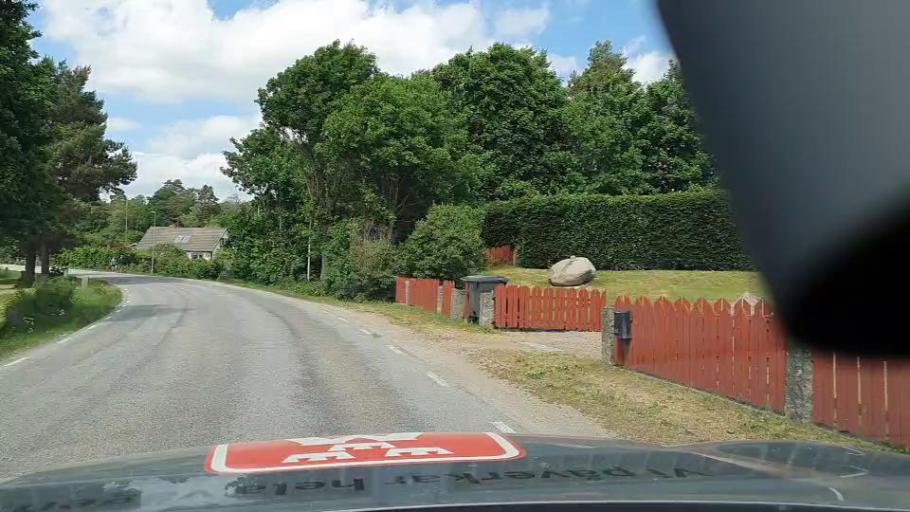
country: SE
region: Blekinge
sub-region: Karlshamns Kommun
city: Morrum
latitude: 56.1102
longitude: 14.6851
